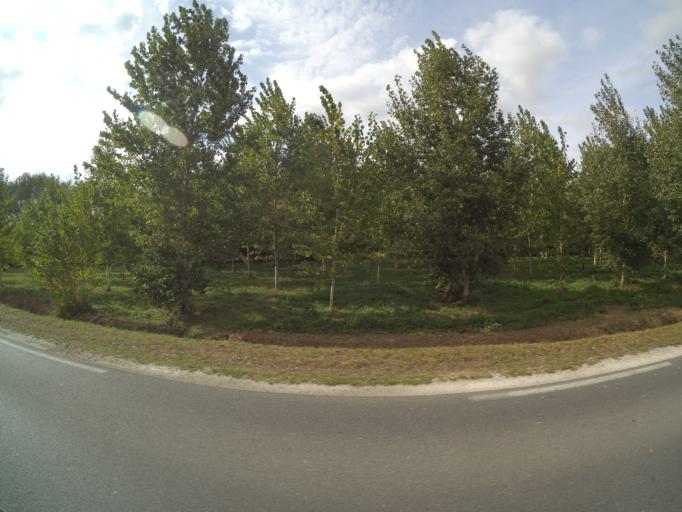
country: FR
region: Centre
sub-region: Departement d'Indre-et-Loire
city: Montlouis-sur-Loire
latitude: 47.4082
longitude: 0.8231
